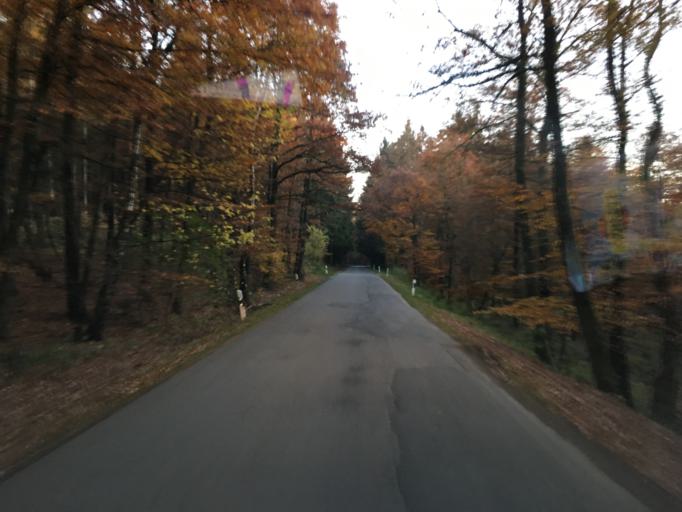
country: DE
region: North Rhine-Westphalia
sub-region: Regierungsbezirk Arnsberg
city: Nachrodt-Wiblingwerde
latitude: 51.2689
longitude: 7.6076
